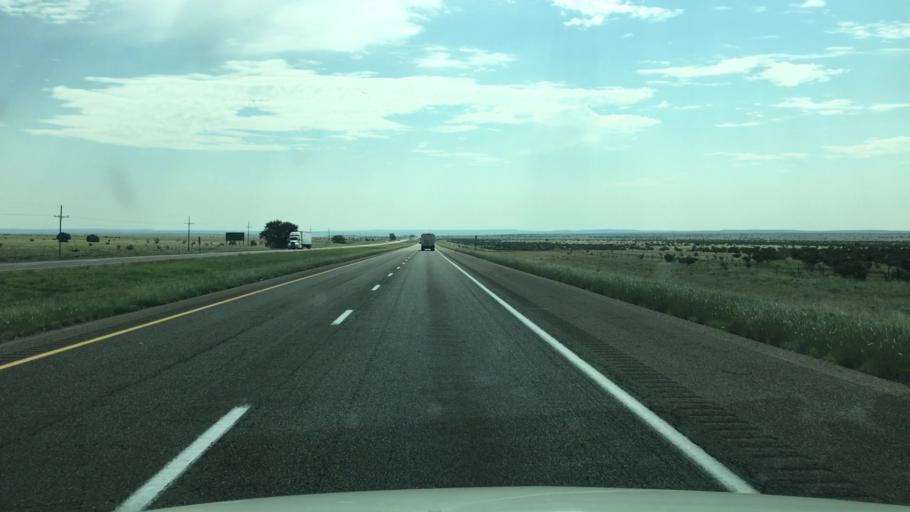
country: US
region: New Mexico
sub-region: Guadalupe County
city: Santa Rosa
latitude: 34.9837
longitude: -105.1384
